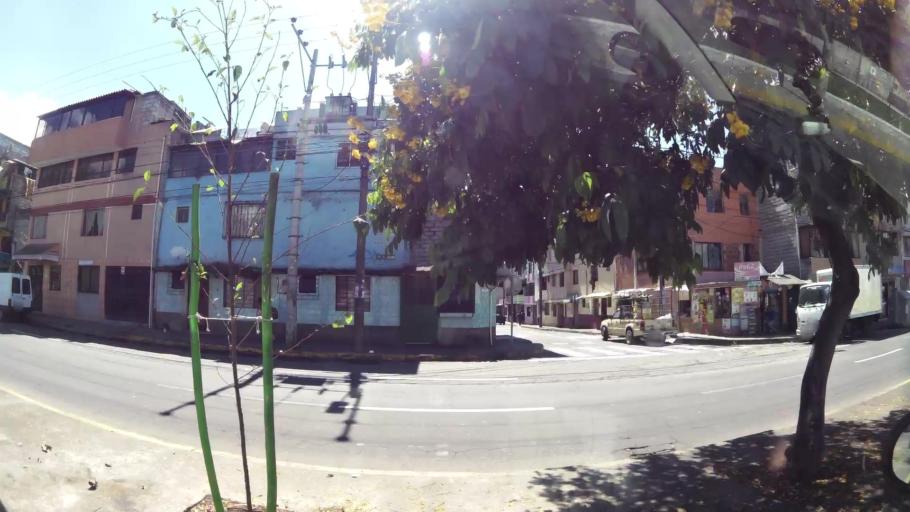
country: EC
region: Pichincha
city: Quito
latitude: -0.2693
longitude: -78.5454
